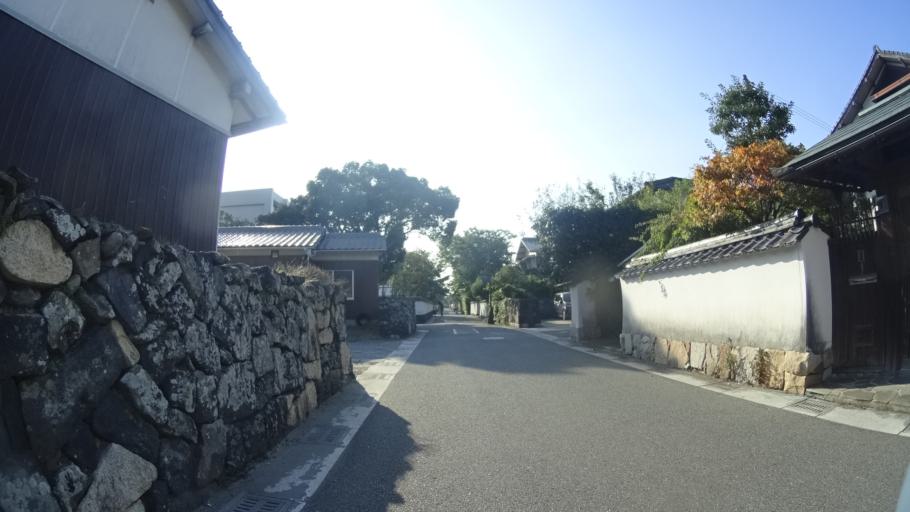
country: JP
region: Yamaguchi
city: Hagi
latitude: 34.4130
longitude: 131.3887
